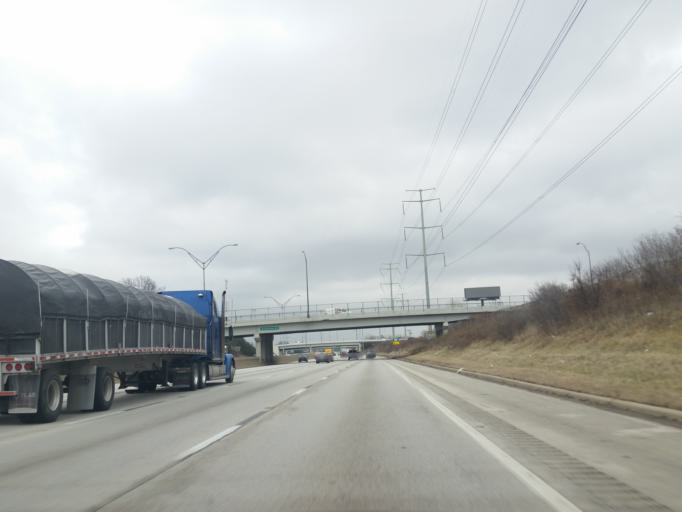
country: US
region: Ohio
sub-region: Cuyahoga County
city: Brooklyn Heights
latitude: 41.4209
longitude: -81.6975
